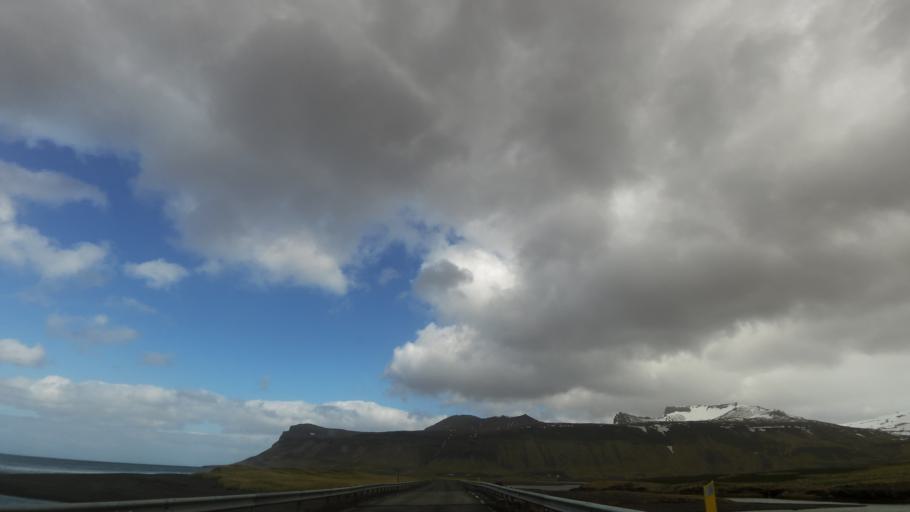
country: IS
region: West
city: Olafsvik
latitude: 64.9185
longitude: -23.5283
